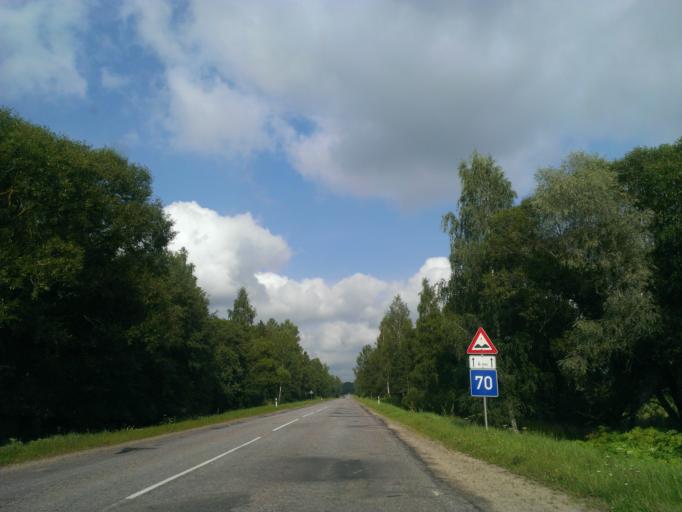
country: LV
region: Priekuli
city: Priekuli
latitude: 57.2660
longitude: 25.4279
